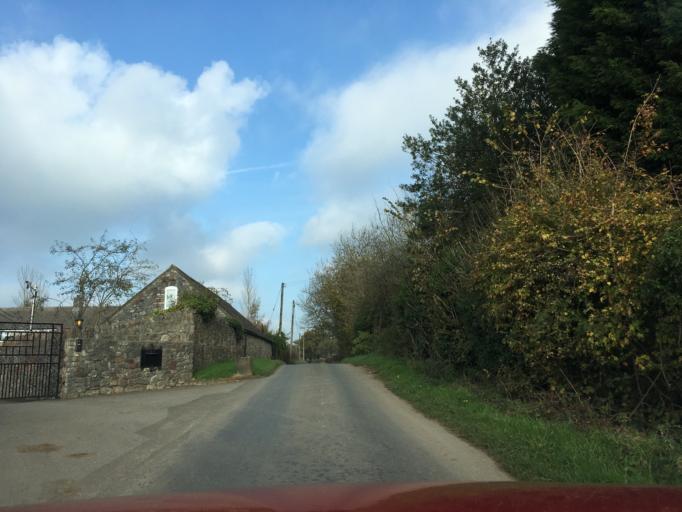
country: GB
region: England
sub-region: South Gloucestershire
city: Yate
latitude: 51.5701
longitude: -2.4253
